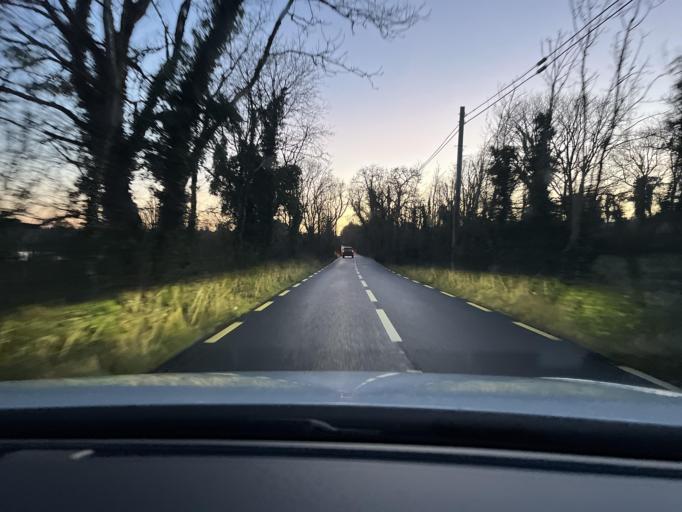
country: IE
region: Connaught
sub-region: County Leitrim
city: Carrick-on-Shannon
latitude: 53.9896
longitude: -8.0391
